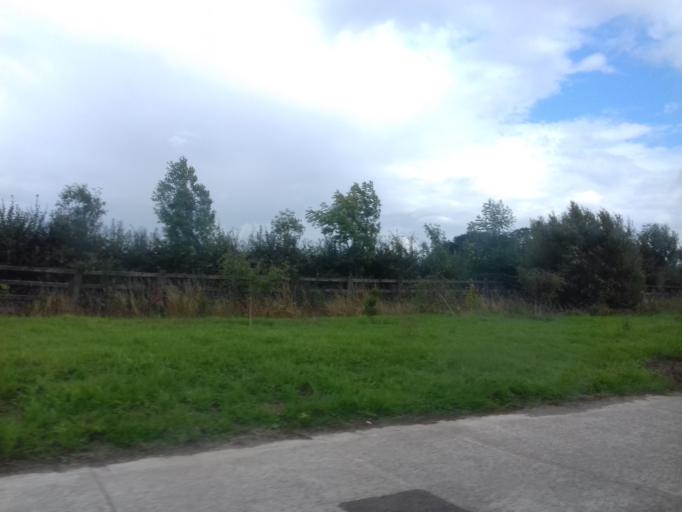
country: IE
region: Munster
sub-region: Waterford
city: Waterford
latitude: 52.2532
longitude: -7.1775
